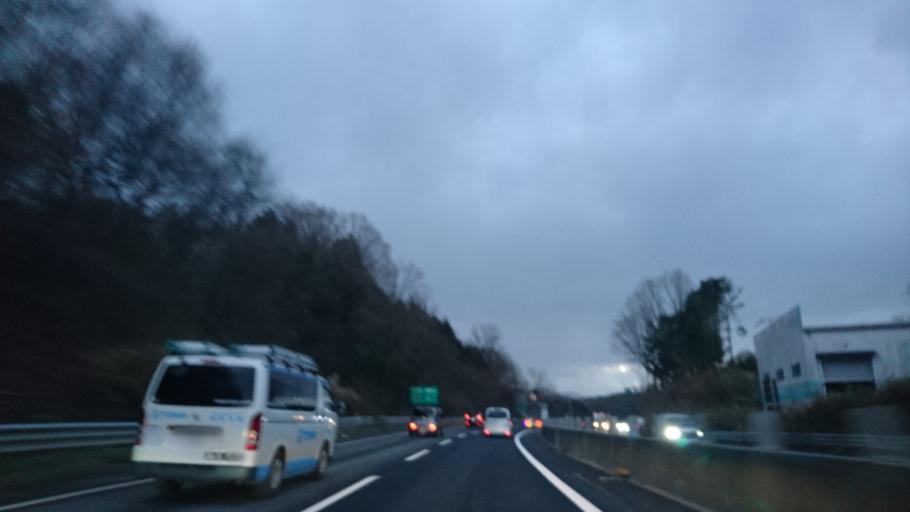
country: JP
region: Nara
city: Haibara-akanedai
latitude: 34.6225
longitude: 135.9828
